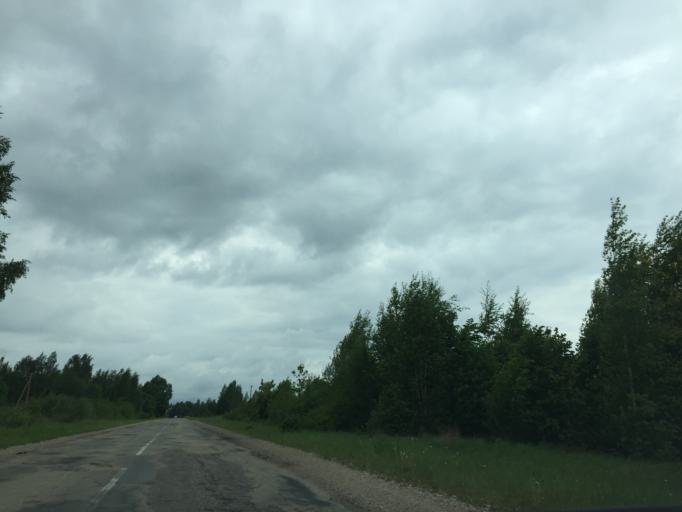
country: LV
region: Varkava
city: Vecvarkava
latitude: 56.0920
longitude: 26.5663
